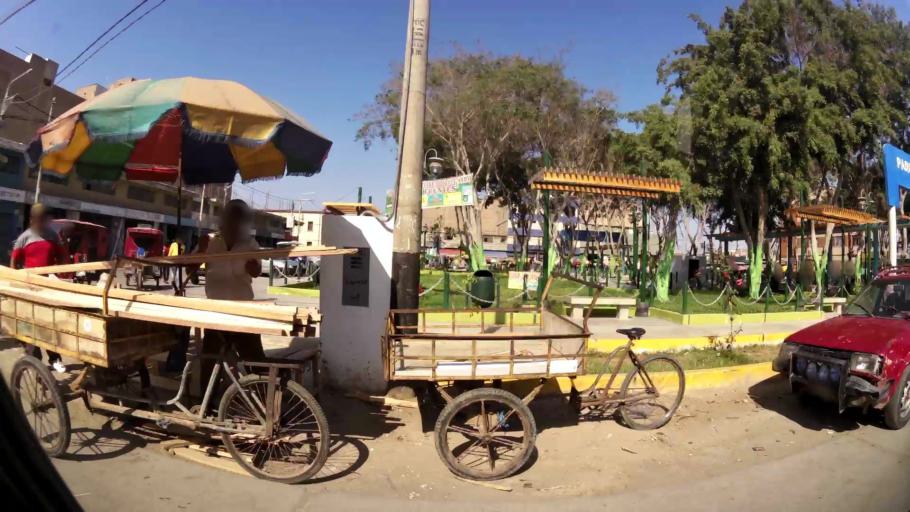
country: PE
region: Lambayeque
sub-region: Provincia de Chiclayo
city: Chiclayo
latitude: -6.7647
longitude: -79.8409
